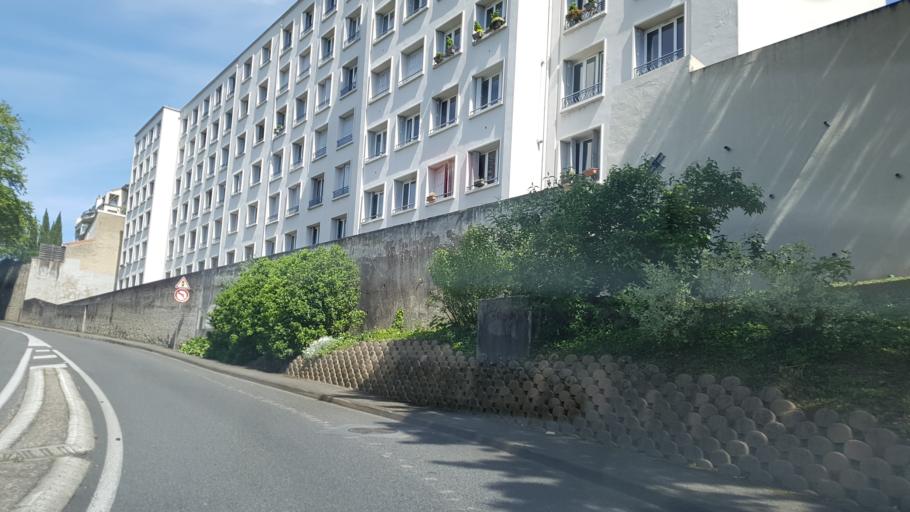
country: FR
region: Rhone-Alpes
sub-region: Departement du Rhone
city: Caluire-et-Cuire
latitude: 45.7982
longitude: 4.8439
